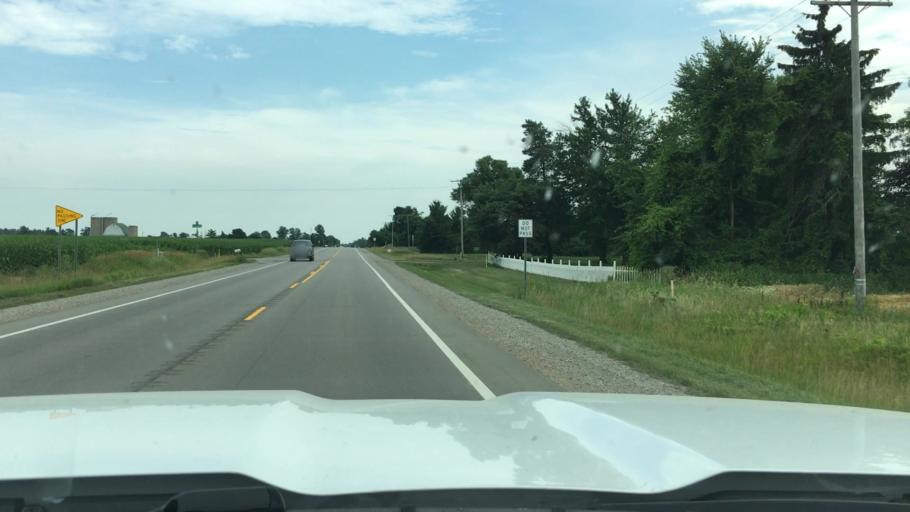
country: US
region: Michigan
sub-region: Sanilac County
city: Marlette
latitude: 43.3648
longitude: -83.0853
